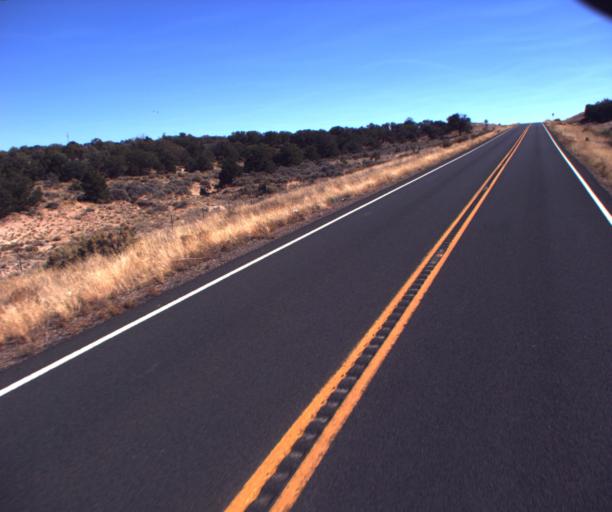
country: US
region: Arizona
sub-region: Apache County
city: Ganado
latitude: 35.7677
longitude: -109.7933
